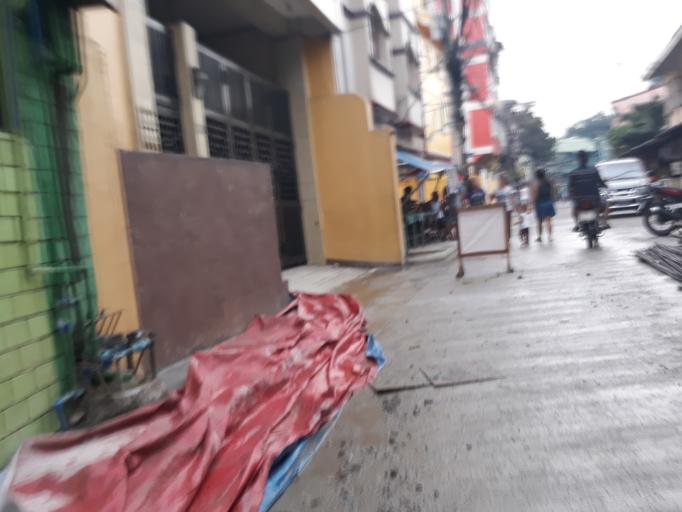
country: PH
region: Metro Manila
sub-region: San Juan
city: San Juan
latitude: 14.6098
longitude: 121.0223
